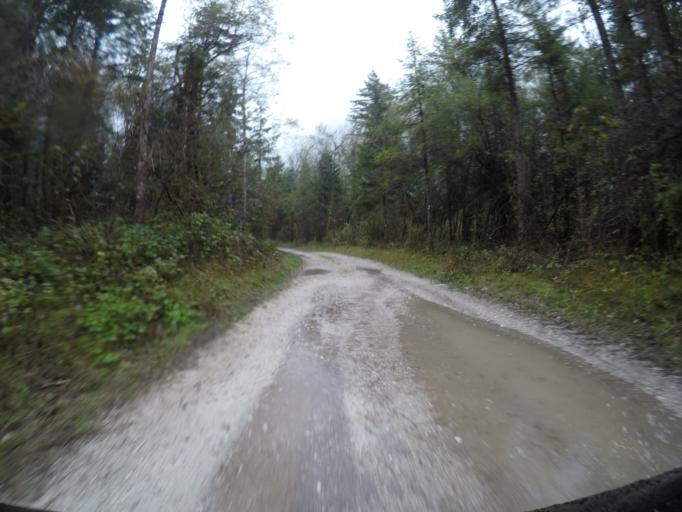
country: SI
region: Bovec
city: Bovec
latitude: 46.3346
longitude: 13.6342
